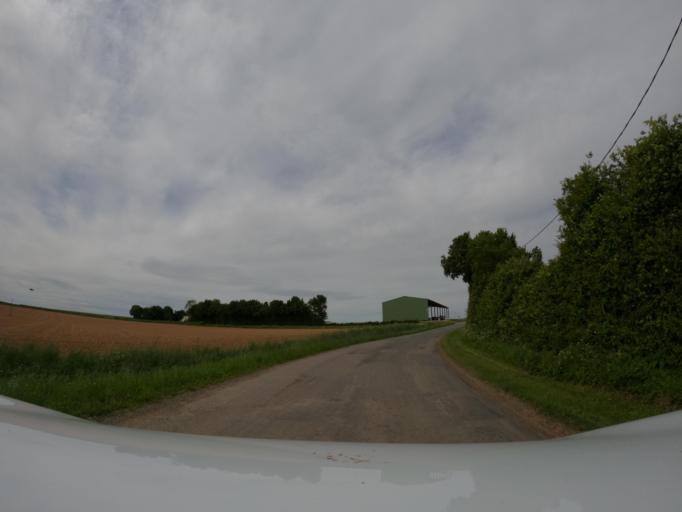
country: FR
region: Pays de la Loire
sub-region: Departement de la Vendee
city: Saint-Hilaire-des-Loges
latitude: 46.4923
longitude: -0.6336
